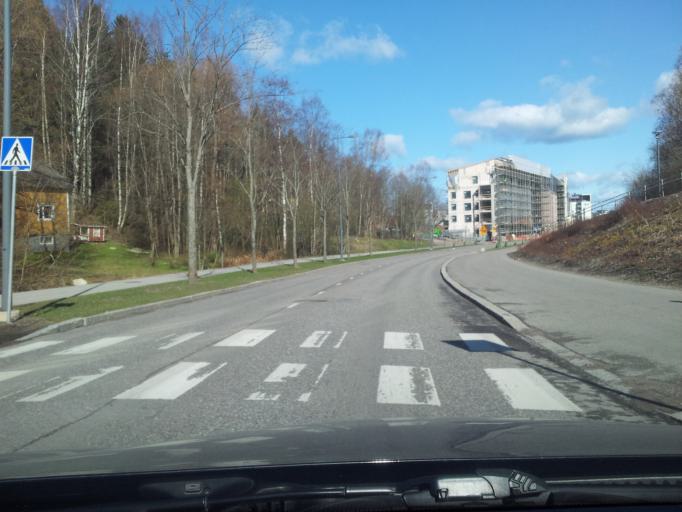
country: FI
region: Uusimaa
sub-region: Helsinki
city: Espoo
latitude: 60.2007
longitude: 24.6627
